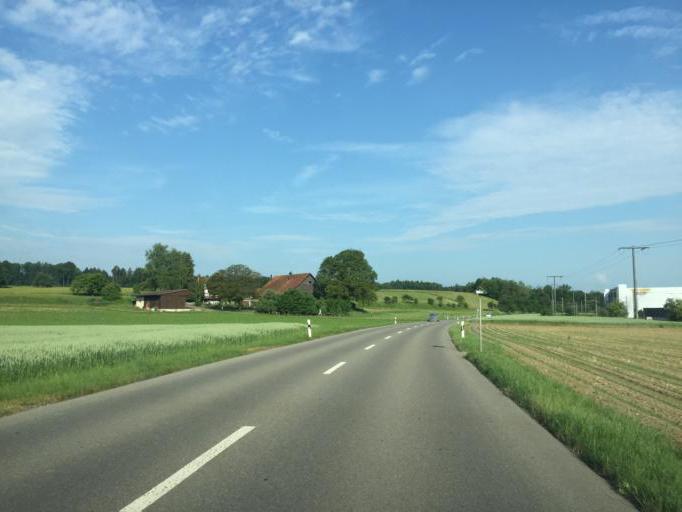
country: CH
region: Zurich
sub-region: Bezirk Dielsdorf
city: Rumlang
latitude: 47.4573
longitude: 8.5247
